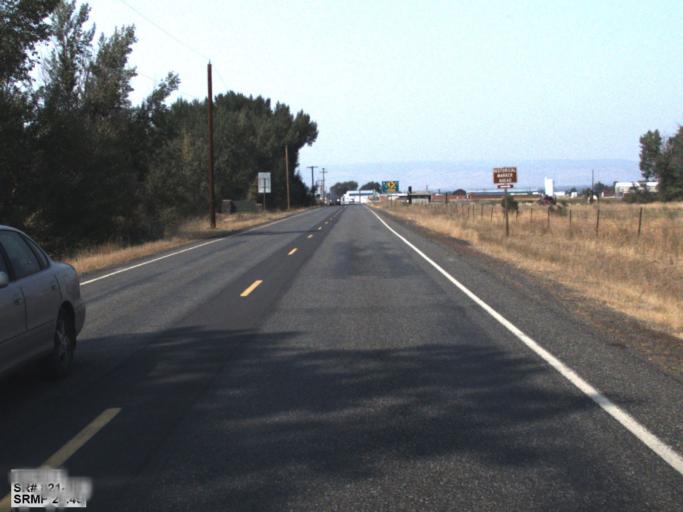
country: US
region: Washington
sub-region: Kittitas County
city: Ellensburg
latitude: 46.9234
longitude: -120.5094
